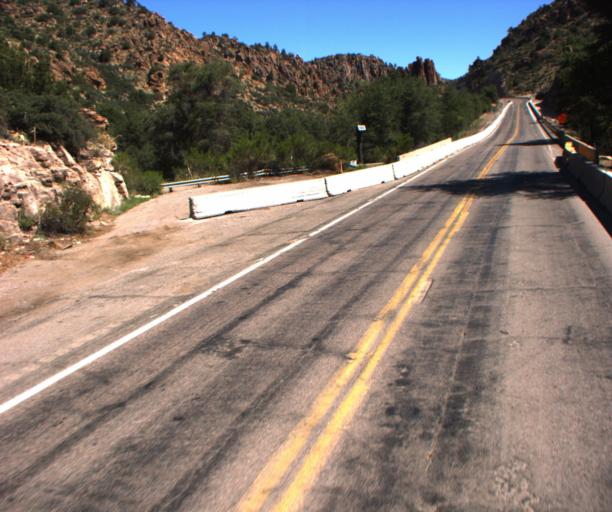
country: US
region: Arizona
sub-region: Pinal County
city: Superior
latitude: 33.3250
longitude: -111.0326
